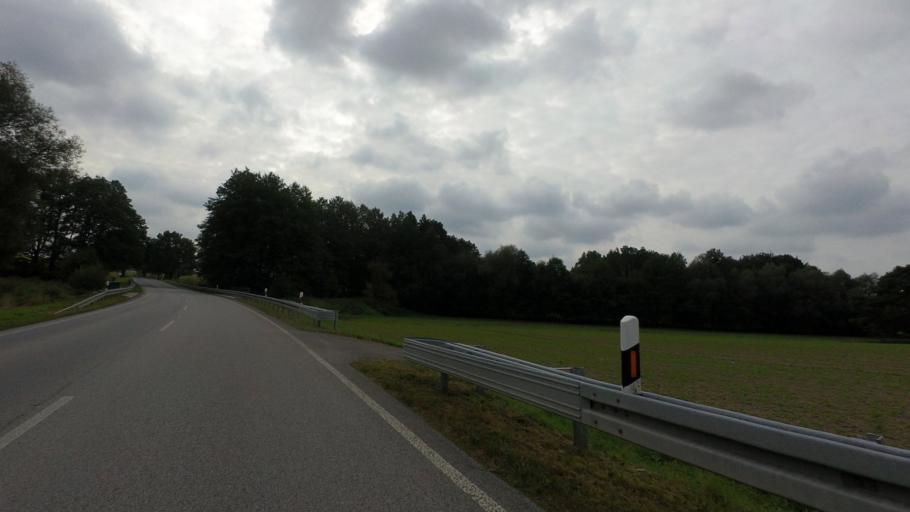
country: DE
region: Brandenburg
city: Luckau
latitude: 51.8141
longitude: 13.6768
